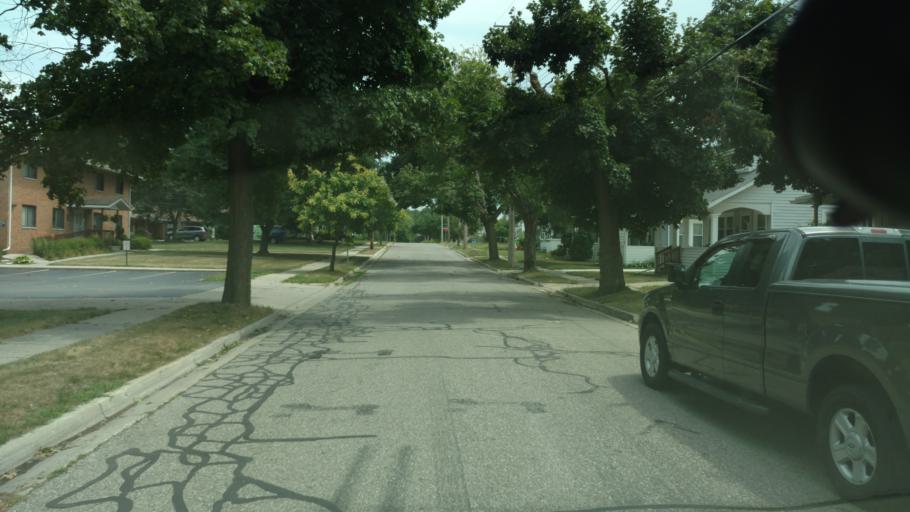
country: US
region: Michigan
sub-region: Ingham County
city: Lansing
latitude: 42.7600
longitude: -84.5533
